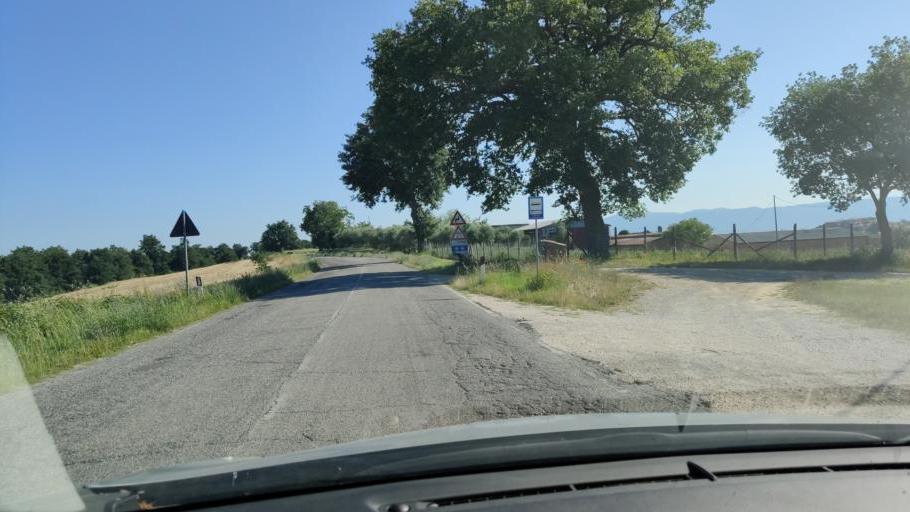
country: IT
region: Umbria
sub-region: Provincia di Terni
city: Avigliano Umbro
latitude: 42.6664
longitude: 12.4408
